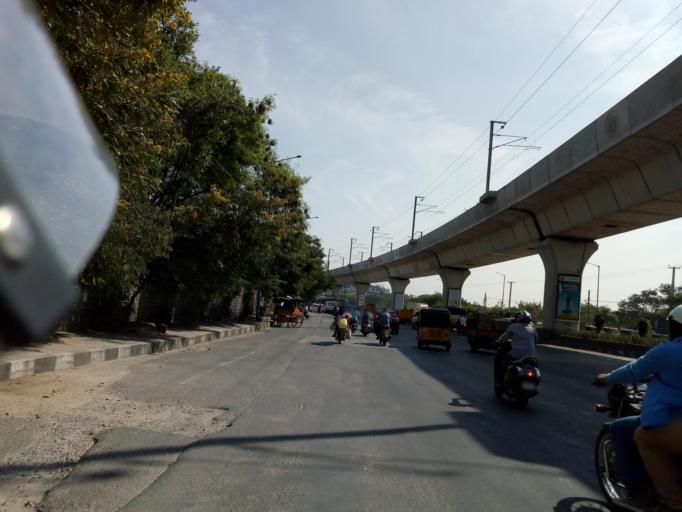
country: IN
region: Telangana
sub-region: Hyderabad
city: Malkajgiri
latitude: 17.4231
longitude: 78.5376
